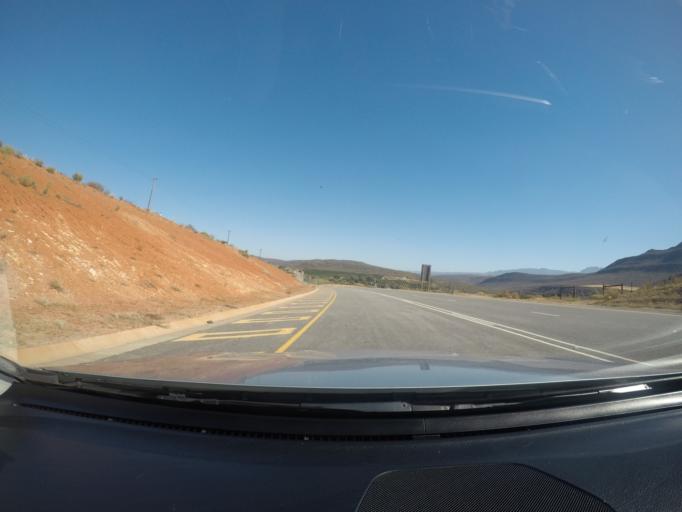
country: ZA
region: Western Cape
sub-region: West Coast District Municipality
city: Clanwilliam
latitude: -32.3675
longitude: 18.9408
